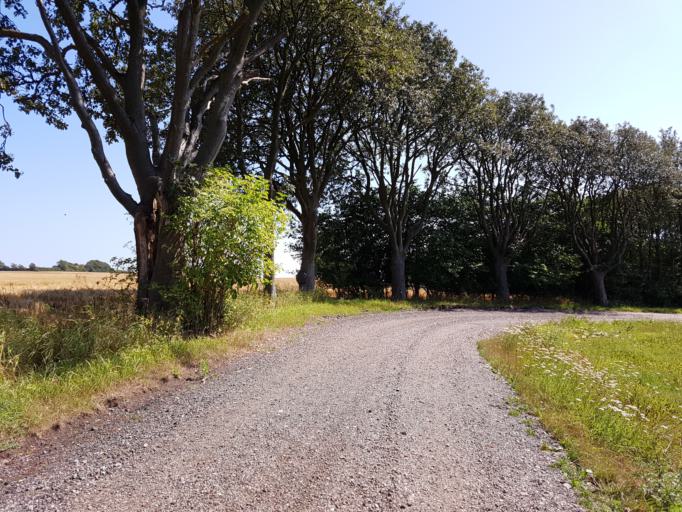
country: DK
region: Zealand
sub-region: Guldborgsund Kommune
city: Nykobing Falster
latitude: 54.5694
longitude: 11.9522
